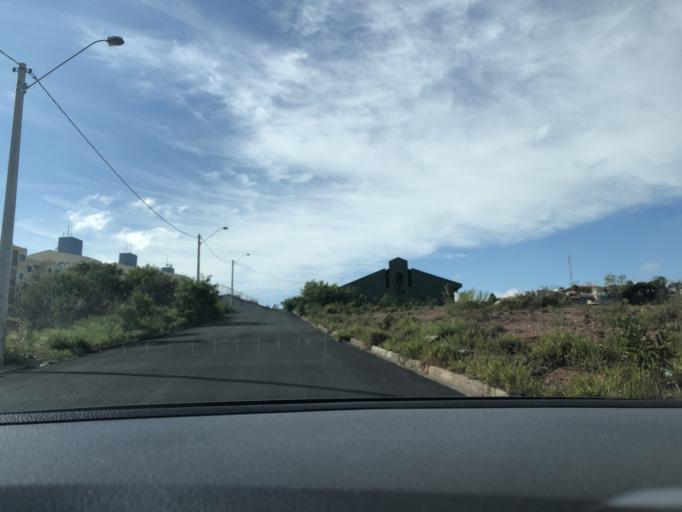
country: BR
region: Sao Paulo
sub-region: Campo Limpo Paulista
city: Campo Limpo Paulista
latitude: -23.2128
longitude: -46.8052
